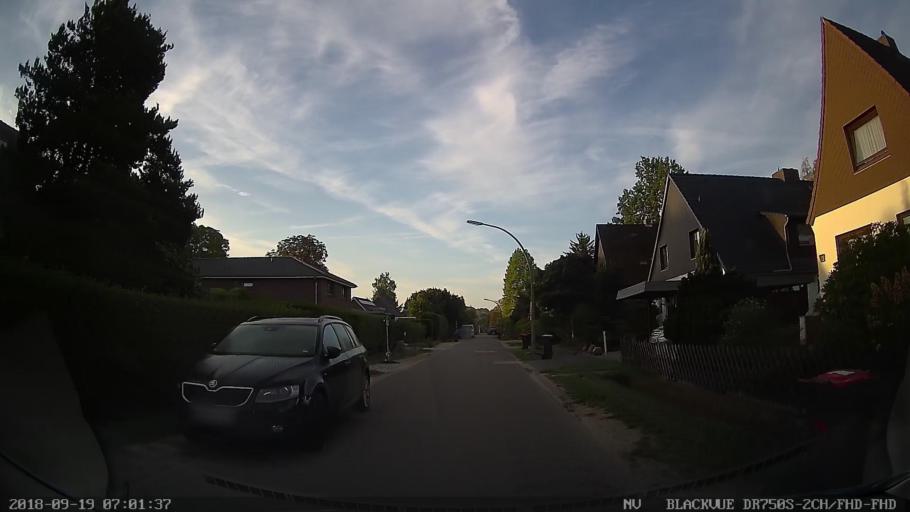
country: DE
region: Hamburg
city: Eidelstedt
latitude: 53.6286
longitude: 9.8987
